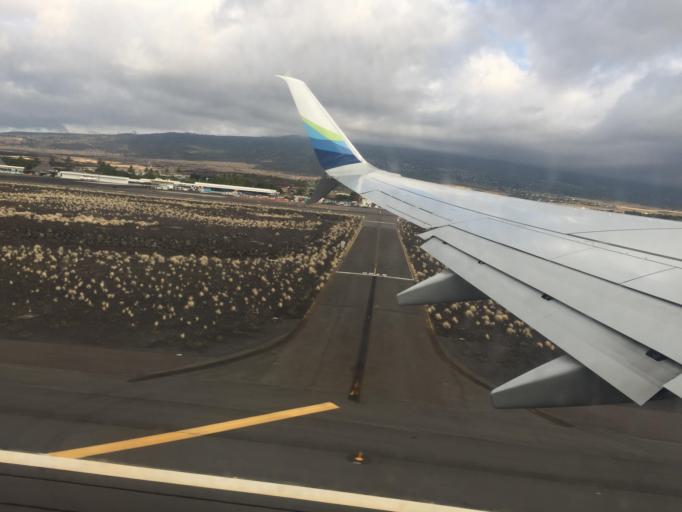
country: US
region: Hawaii
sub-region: Hawaii County
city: Kalaoa
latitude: 19.7324
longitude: -156.0462
